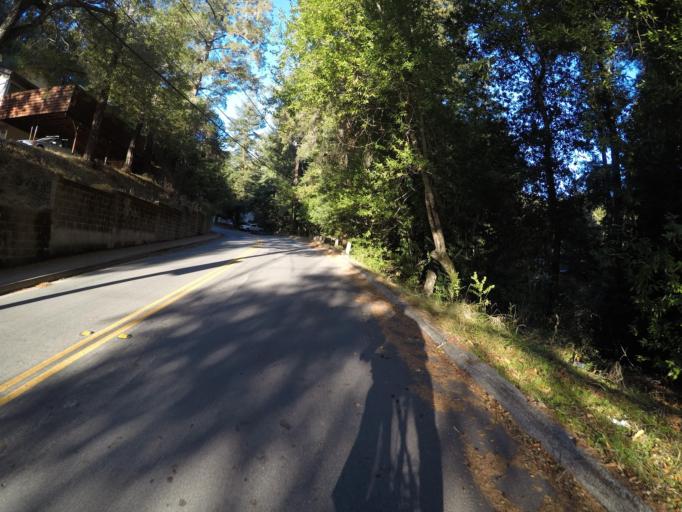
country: US
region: California
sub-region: Santa Cruz County
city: Scotts Valley
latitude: 37.0698
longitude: -121.9956
